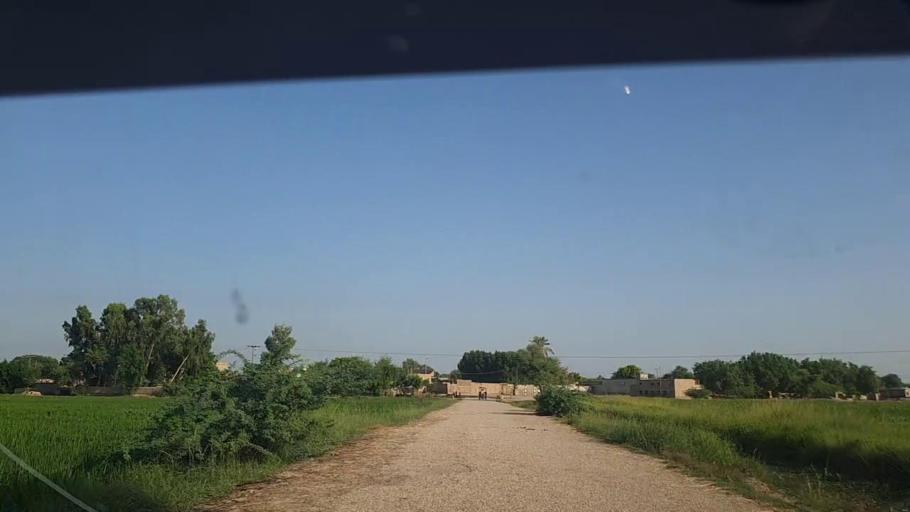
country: PK
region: Sindh
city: Tangwani
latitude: 28.2655
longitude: 69.0135
